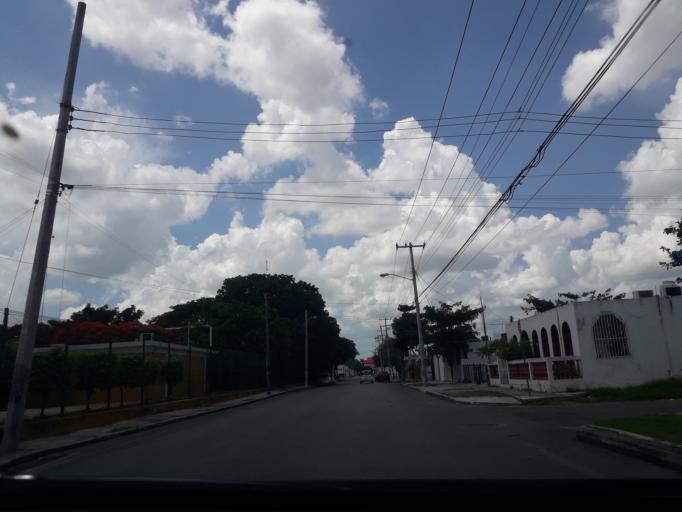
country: MX
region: Yucatan
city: Merida
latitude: 20.9811
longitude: -89.6550
